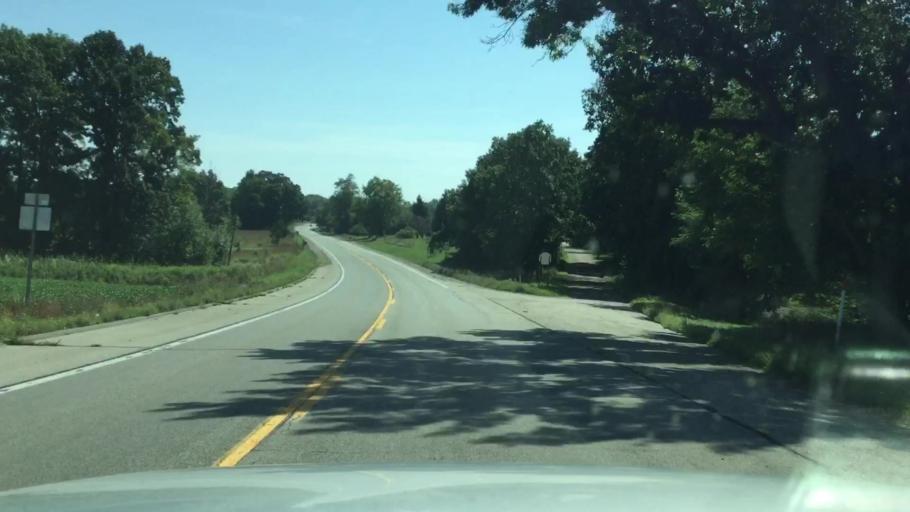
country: US
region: Michigan
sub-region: Lenawee County
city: Manitou Beach-Devils Lake
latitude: 42.0098
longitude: -84.3018
